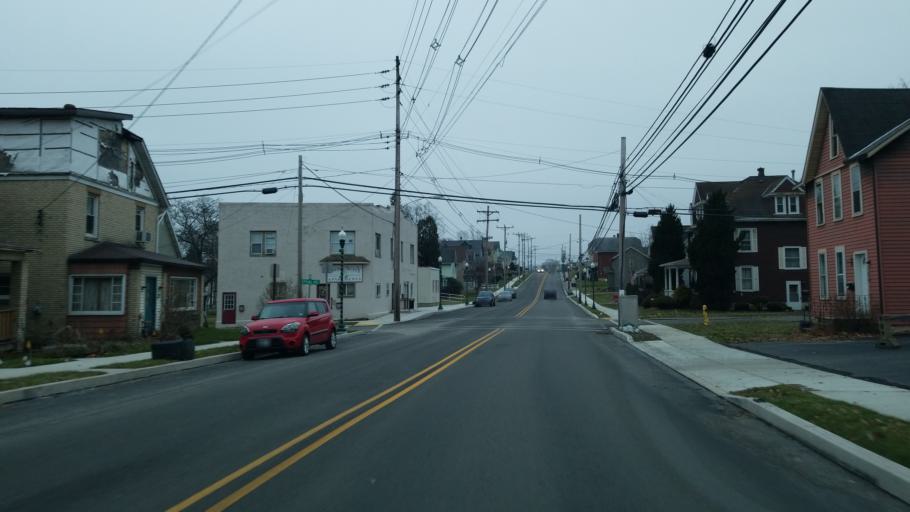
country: US
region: Pennsylvania
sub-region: Clearfield County
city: Sandy
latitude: 41.1167
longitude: -78.7705
